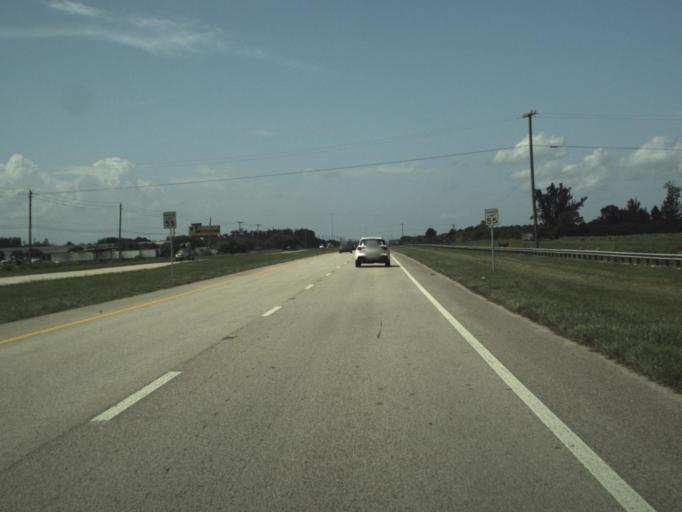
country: US
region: Florida
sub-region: Palm Beach County
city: Villages of Oriole
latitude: 26.4844
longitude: -80.2047
